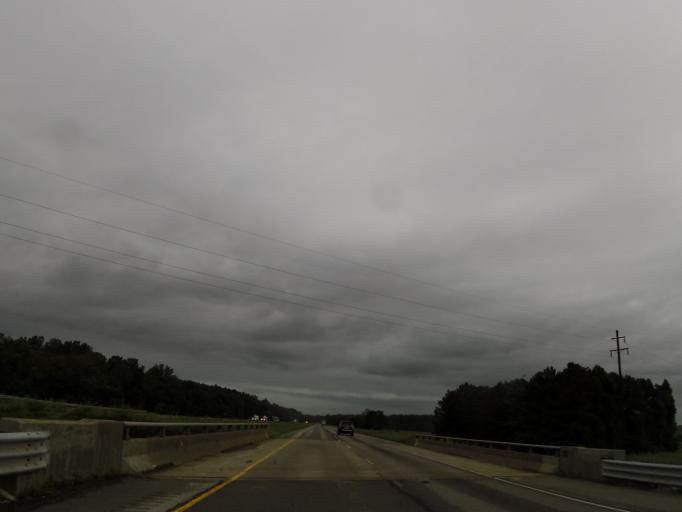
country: US
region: Illinois
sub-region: Massac County
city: Metropolis
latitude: 37.3014
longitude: -88.7532
